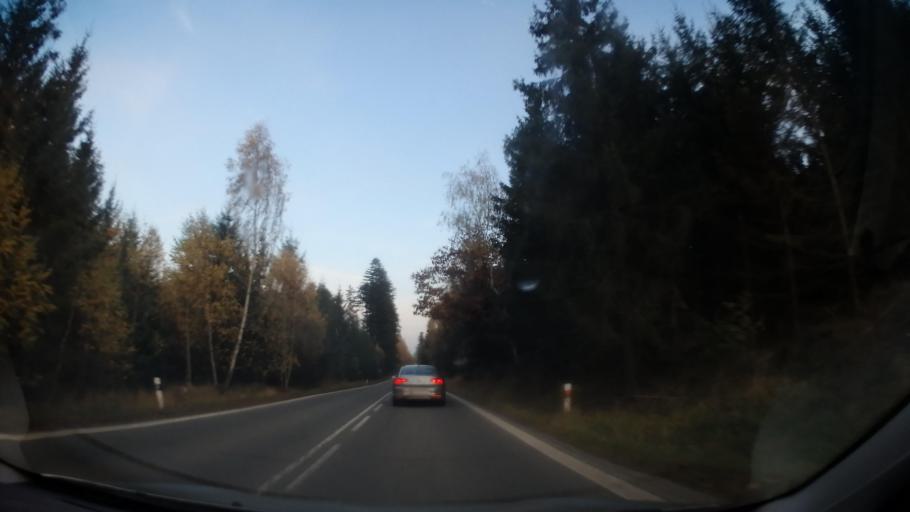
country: CZ
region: Vysocina
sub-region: Okres Pelhrimov
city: Zeliv
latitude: 49.5494
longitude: 15.1434
